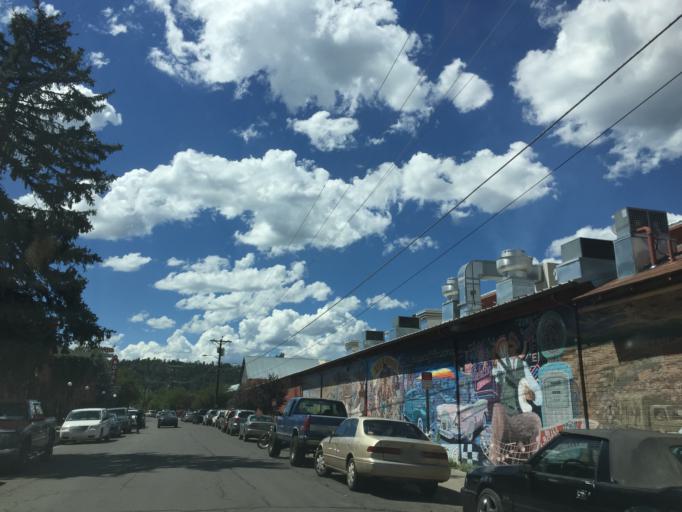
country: US
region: Arizona
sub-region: Coconino County
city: Flagstaff
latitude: 35.1963
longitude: -111.6486
